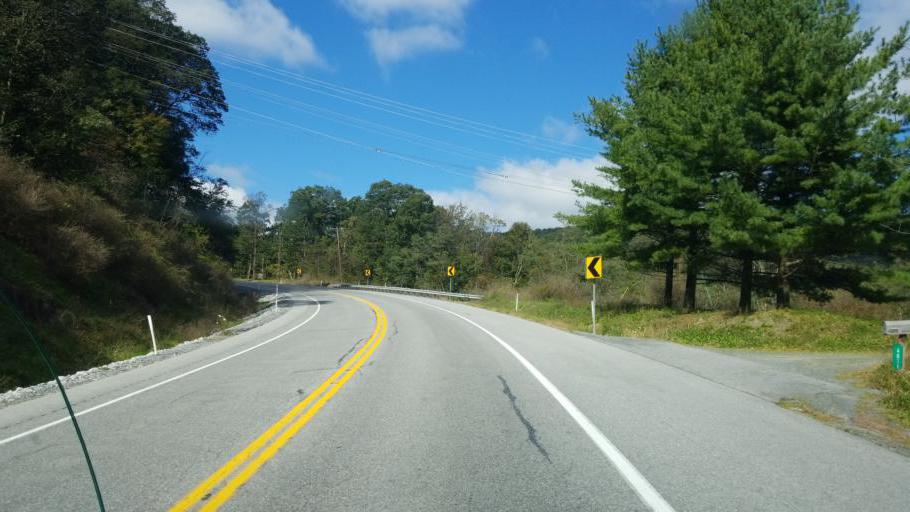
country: US
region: Pennsylvania
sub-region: Fulton County
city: McConnellsburg
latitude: 40.0164
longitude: -78.1196
